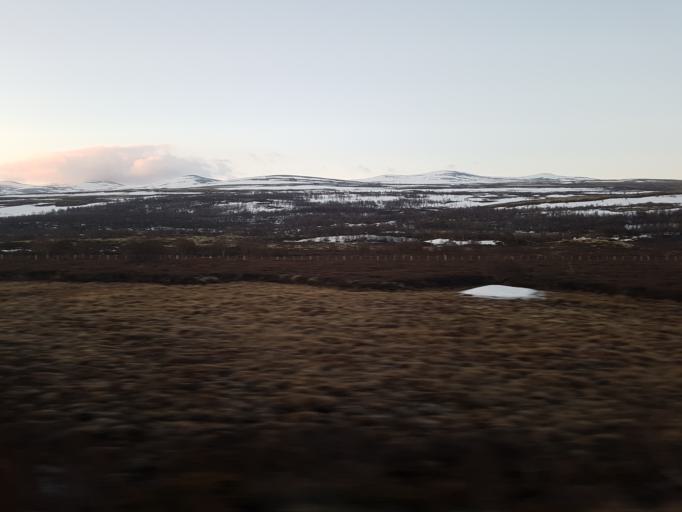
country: NO
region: Oppland
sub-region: Dovre
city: Dovre
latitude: 62.1108
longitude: 9.2631
